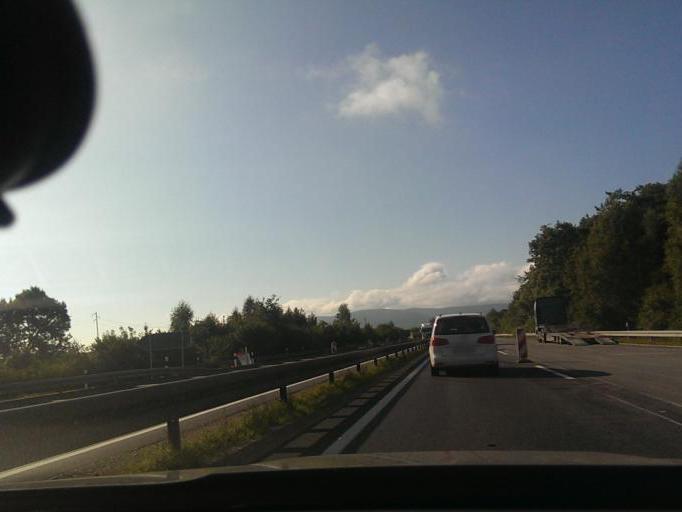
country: DE
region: Lower Saxony
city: Vienenburg
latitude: 51.9464
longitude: 10.5849
